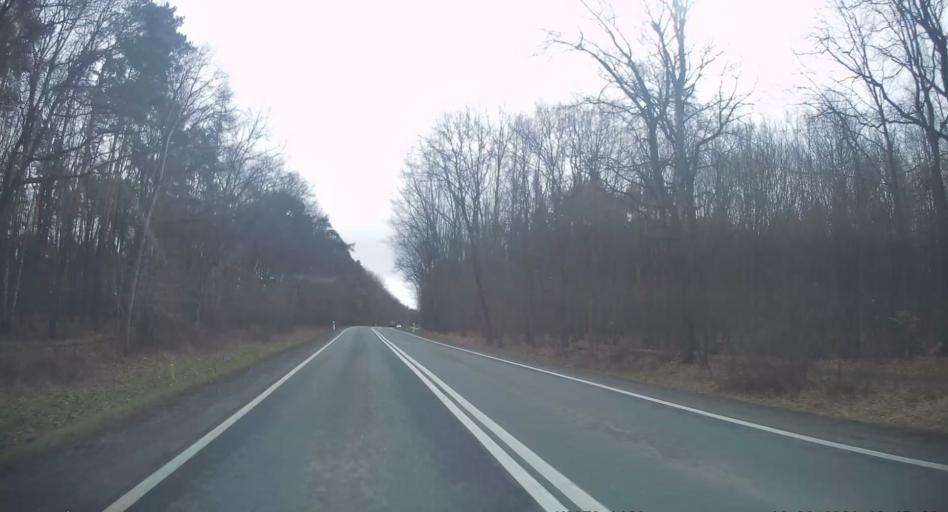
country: PL
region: Lesser Poland Voivodeship
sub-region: Powiat wielicki
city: Szarow
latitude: 50.0139
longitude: 20.2453
